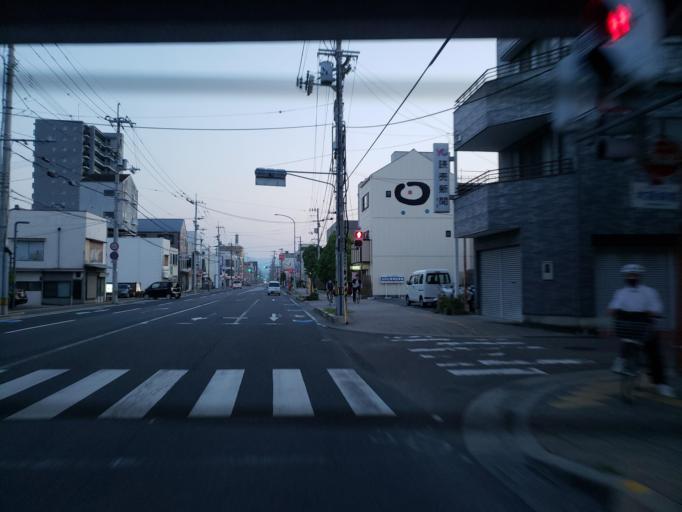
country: JP
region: Ehime
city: Hojo
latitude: 34.0622
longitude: 132.9955
